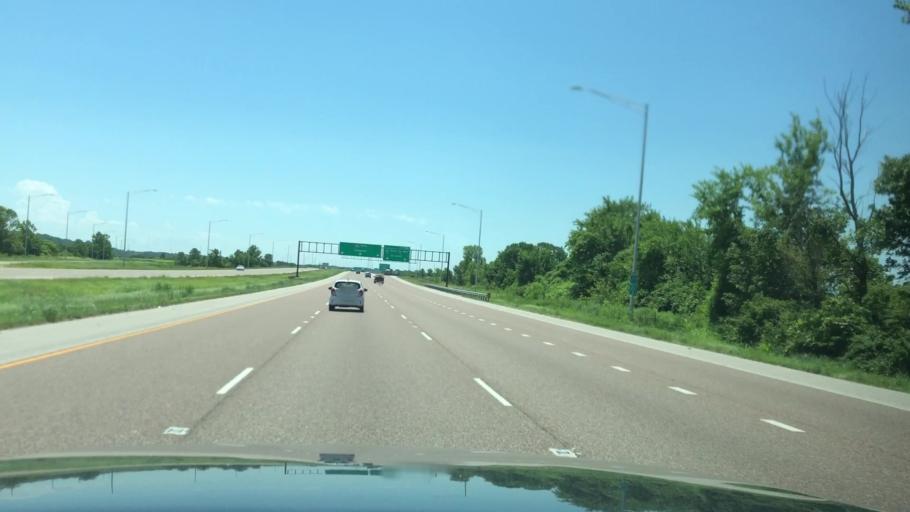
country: US
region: Illinois
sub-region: Saint Clair County
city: Caseyville
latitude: 38.6831
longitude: -90.0304
